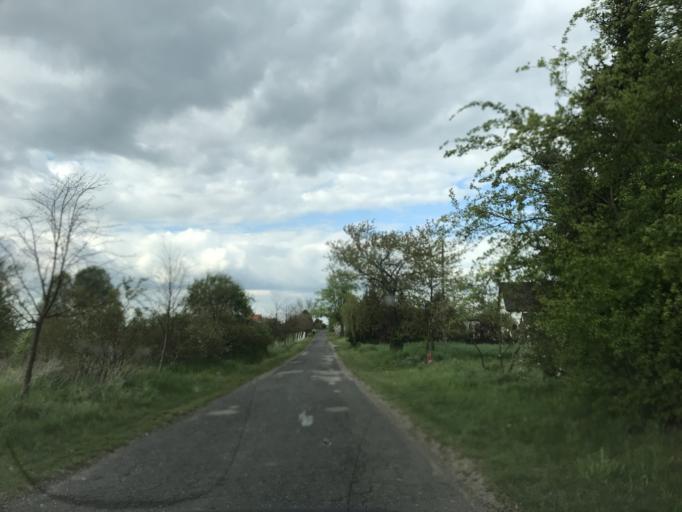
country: PL
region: West Pomeranian Voivodeship
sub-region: Powiat mysliborski
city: Mysliborz
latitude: 52.8910
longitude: 14.8987
